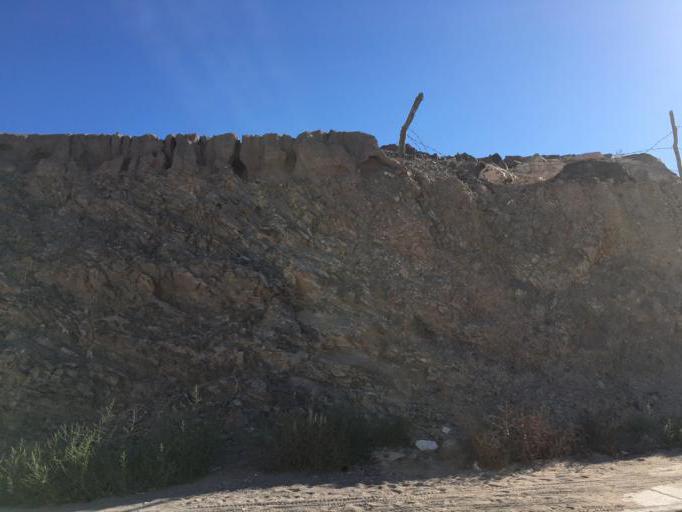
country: MX
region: Sonora
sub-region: Puerto Penasco
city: Puerto Penasco
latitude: 31.3030
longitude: -113.5460
